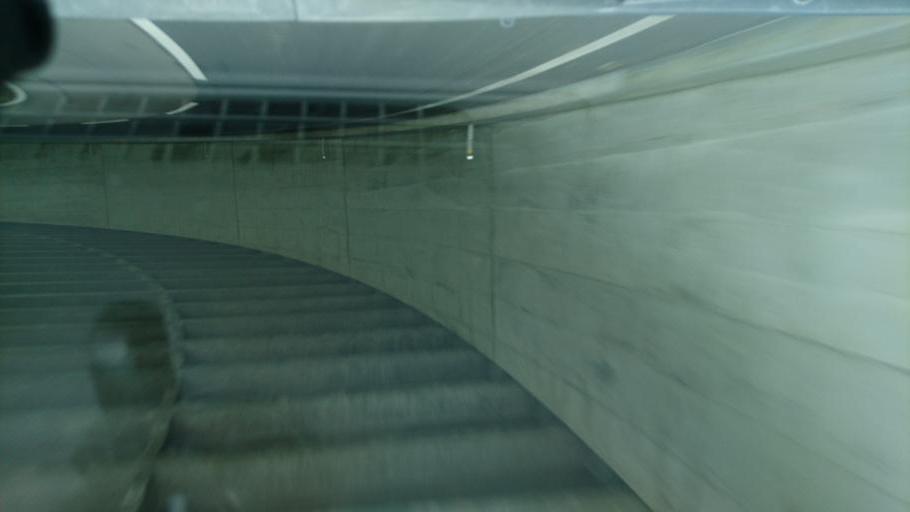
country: JP
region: Akita
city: Yuzawa
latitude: 39.1662
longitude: 140.7447
